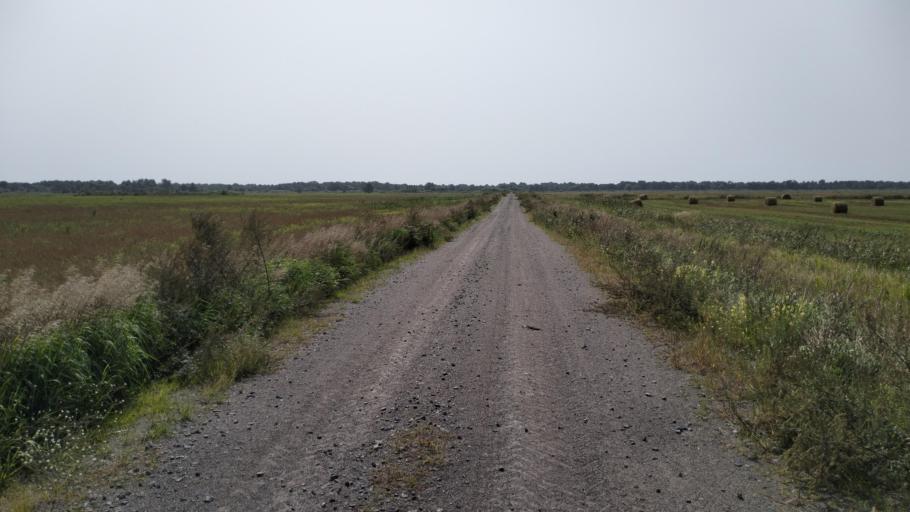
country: BY
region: Brest
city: Davyd-Haradok
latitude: 51.9785
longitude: 27.1745
